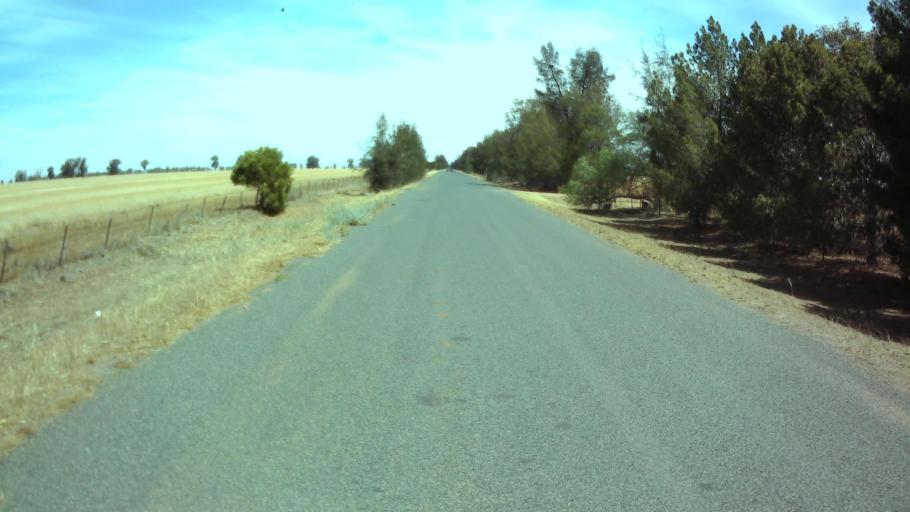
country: AU
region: New South Wales
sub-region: Weddin
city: Grenfell
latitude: -33.9156
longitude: 147.7651
